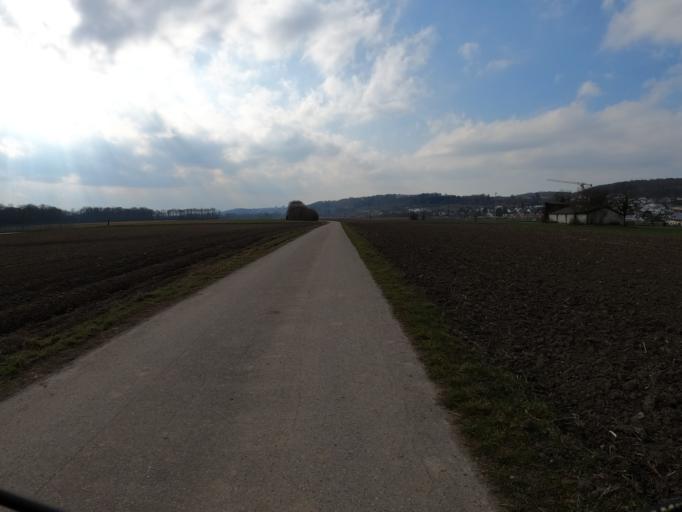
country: DE
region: Bavaria
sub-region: Swabia
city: Nersingen
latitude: 48.4451
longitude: 10.0863
